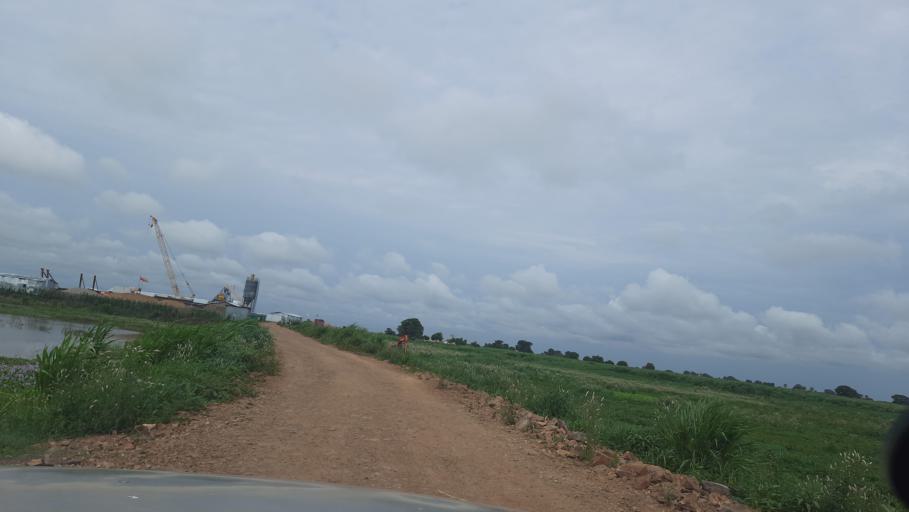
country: ET
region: Gambela
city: Gambela
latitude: 8.3562
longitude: 33.7922
